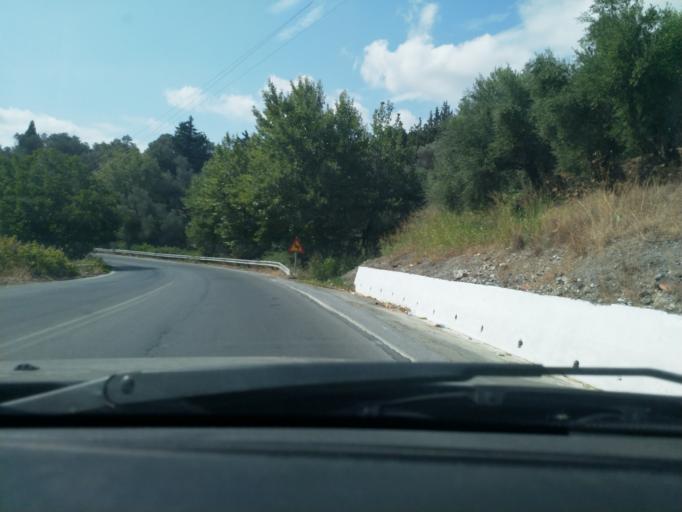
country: GR
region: Crete
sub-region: Nomos Rethymnis
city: Agia Foteini
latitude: 35.2206
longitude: 24.5187
